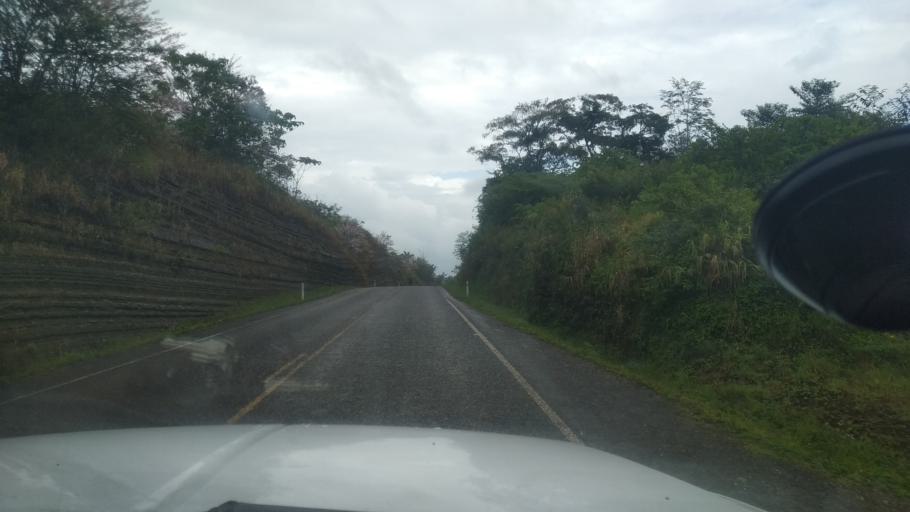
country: GT
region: Peten
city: San Luis
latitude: 16.1855
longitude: -89.1955
